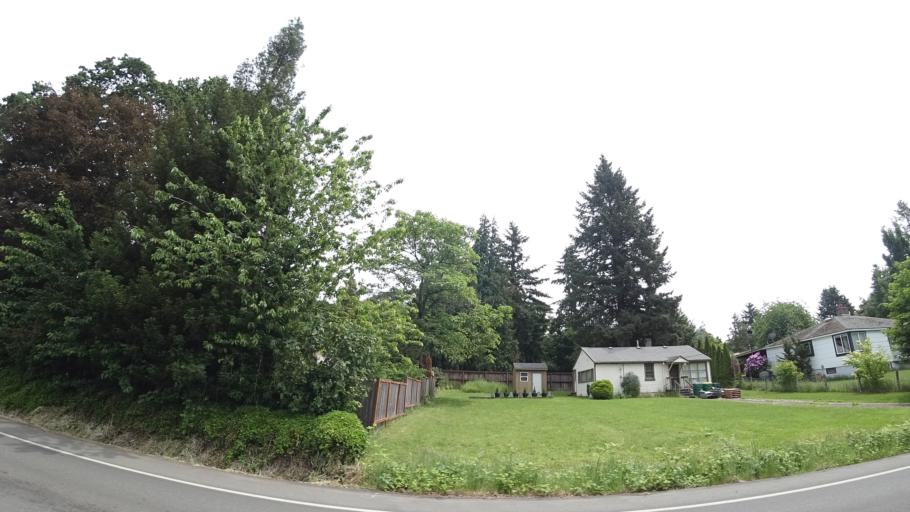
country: US
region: Oregon
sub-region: Washington County
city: Metzger
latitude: 45.4464
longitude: -122.7591
